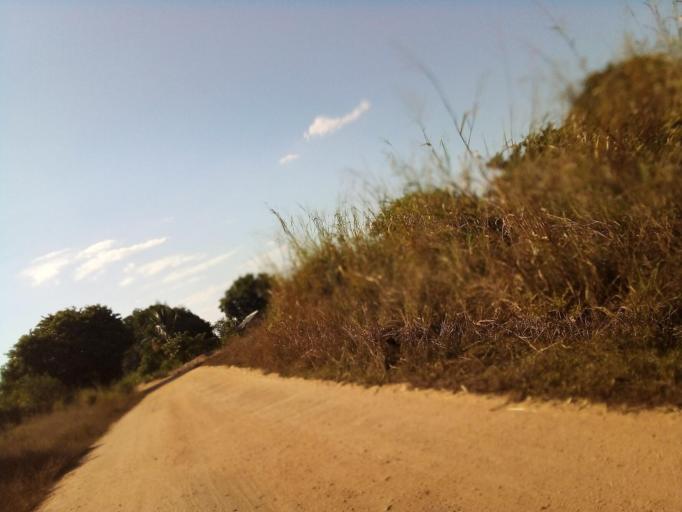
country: MZ
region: Zambezia
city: Quelimane
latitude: -17.5715
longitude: 36.6399
